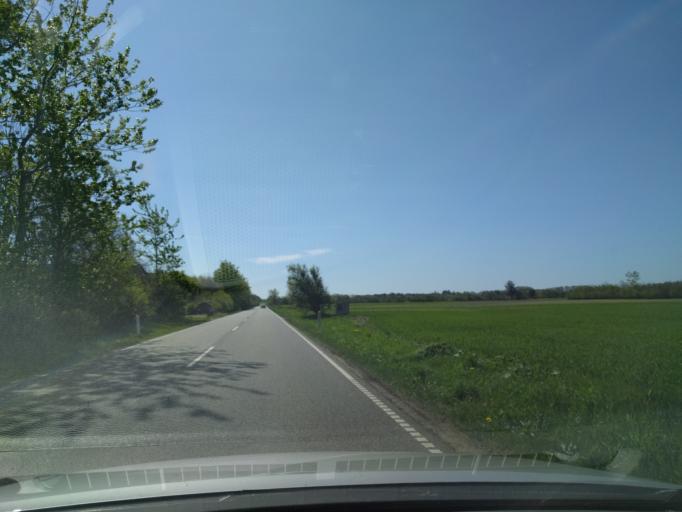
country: DK
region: Central Jutland
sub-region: Ringkobing-Skjern Kommune
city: Tarm
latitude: 55.8810
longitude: 8.5266
